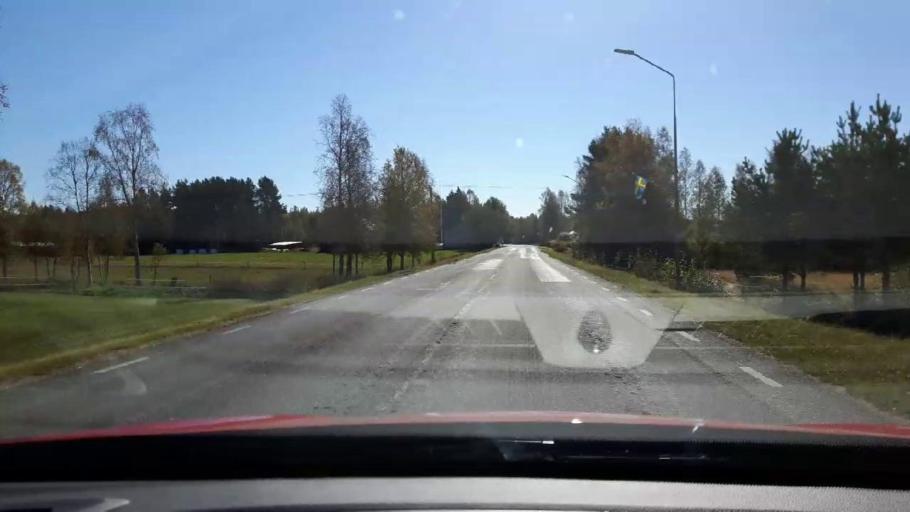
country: SE
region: Jaemtland
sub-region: Harjedalens Kommun
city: Sveg
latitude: 62.3119
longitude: 14.0386
